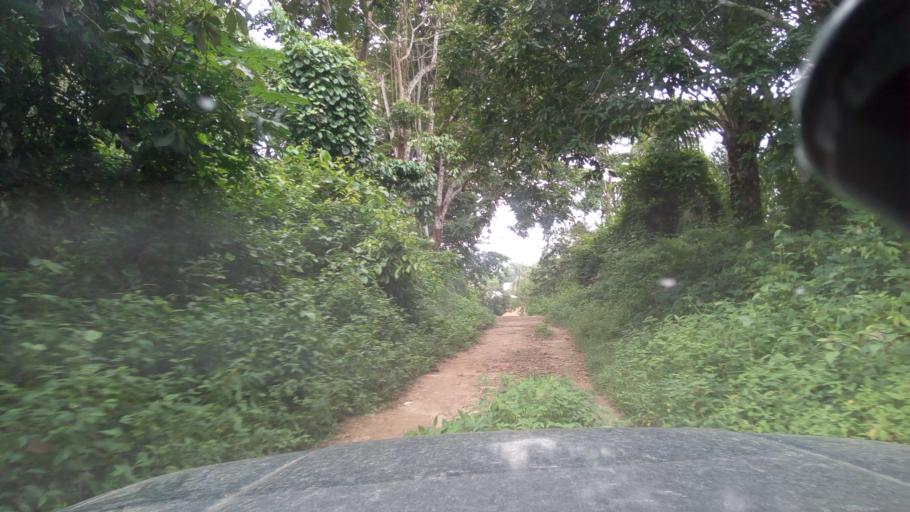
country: SL
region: Eastern Province
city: Segbwema
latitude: 8.1043
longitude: -11.0131
